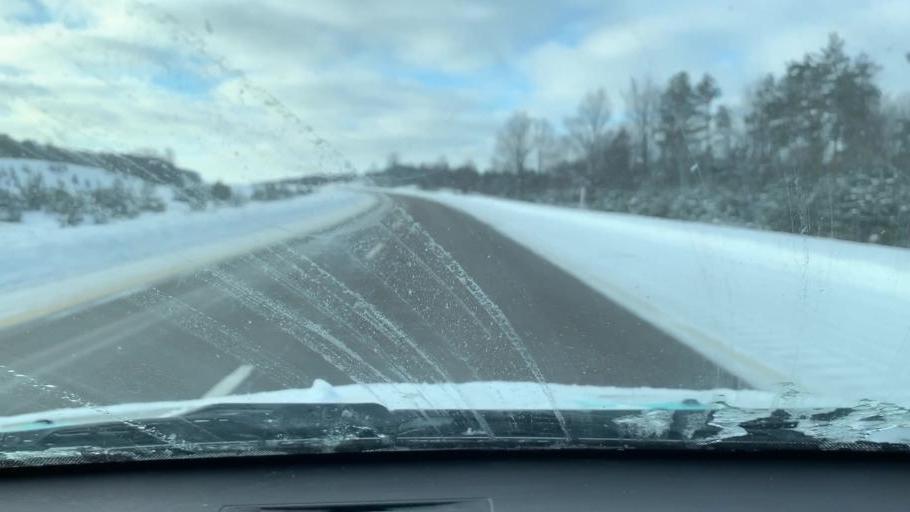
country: US
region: Michigan
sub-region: Wexford County
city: Manton
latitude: 44.3688
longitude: -85.4016
